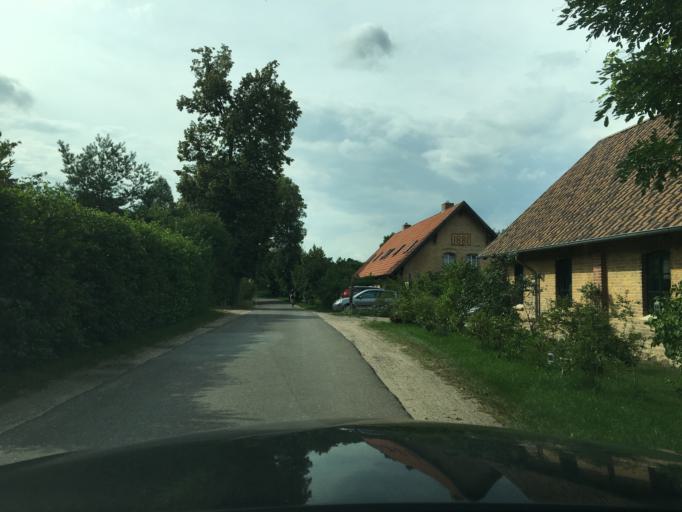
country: DE
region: Mecklenburg-Vorpommern
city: Waren
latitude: 53.4632
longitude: 12.7994
